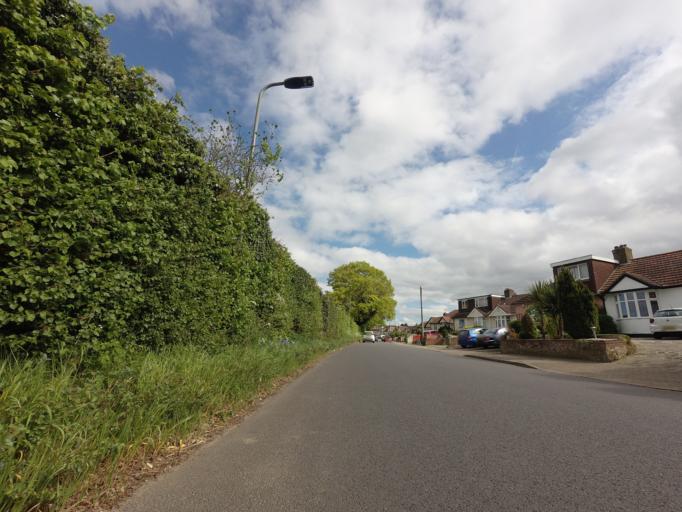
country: GB
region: England
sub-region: Greater London
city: Orpington
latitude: 51.3824
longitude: 0.1226
